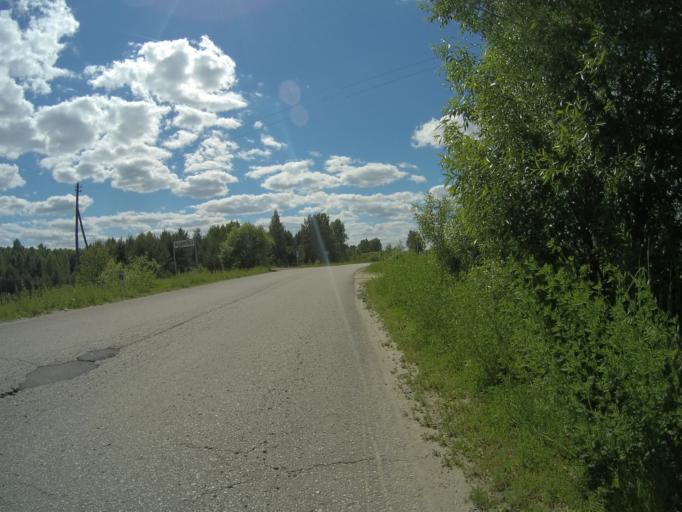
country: RU
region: Vladimir
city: Sudogda
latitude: 56.0795
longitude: 40.7736
